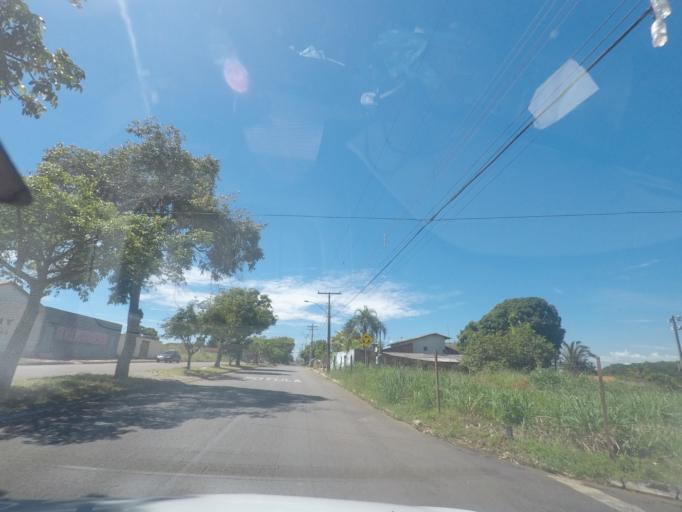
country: BR
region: Goias
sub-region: Aparecida De Goiania
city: Aparecida de Goiania
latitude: -16.7786
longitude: -49.3382
